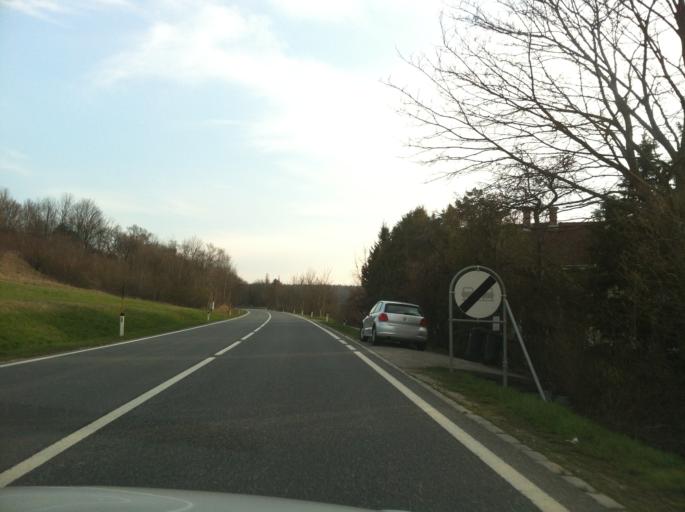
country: AT
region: Lower Austria
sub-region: Politischer Bezirk Tulln
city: Tulbing
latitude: 48.2534
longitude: 16.0884
